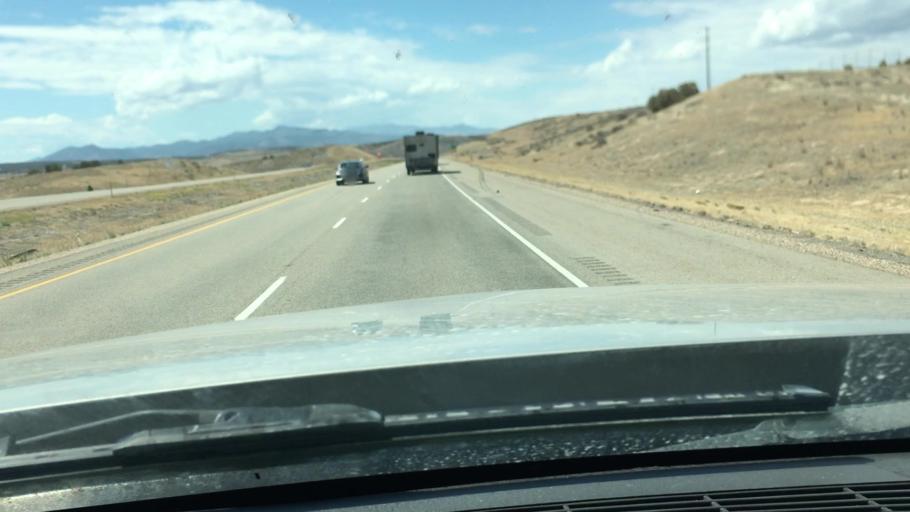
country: US
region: Utah
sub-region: Juab County
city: Nephi
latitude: 39.5062
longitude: -111.9644
